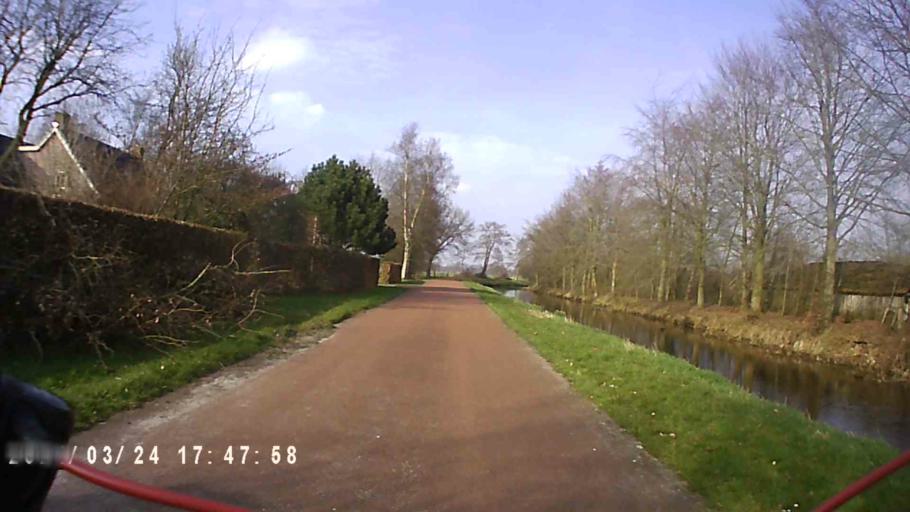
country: NL
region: Groningen
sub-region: Gemeente Leek
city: Leek
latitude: 53.1167
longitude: 6.3354
